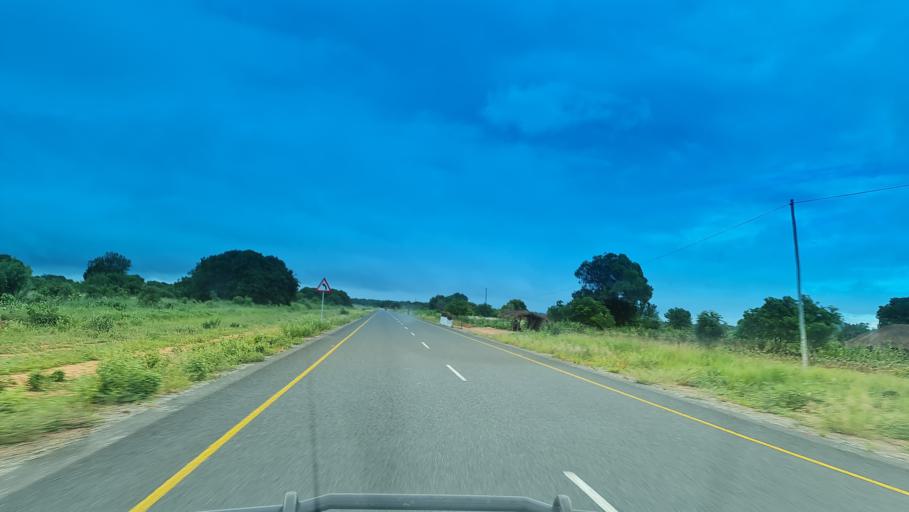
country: MZ
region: Nampula
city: Nampula
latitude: -15.5765
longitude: 39.3234
